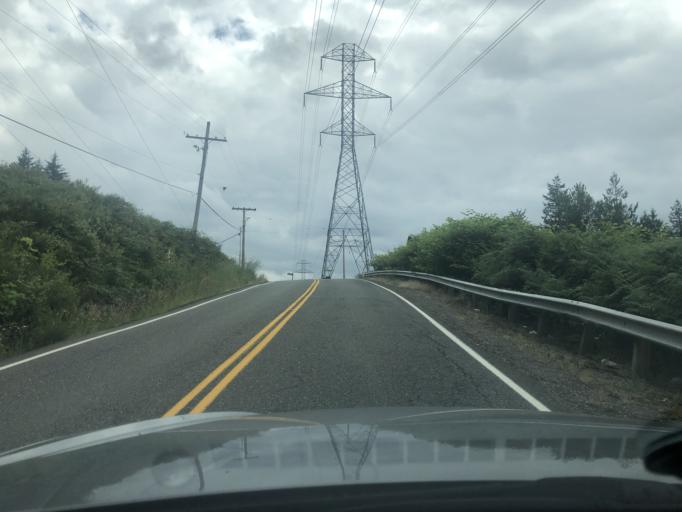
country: US
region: Washington
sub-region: King County
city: Lea Hill
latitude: 47.3031
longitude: -122.1450
